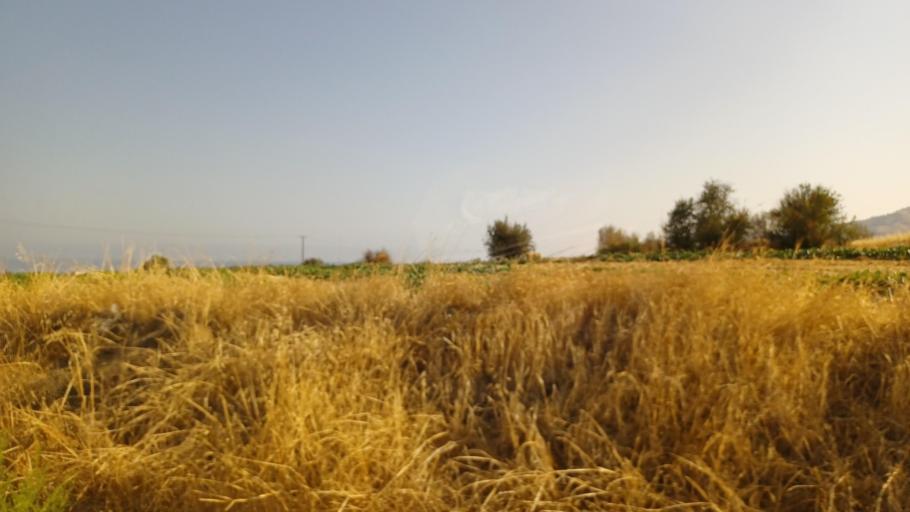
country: CY
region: Pafos
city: Polis
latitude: 35.0556
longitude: 32.4734
